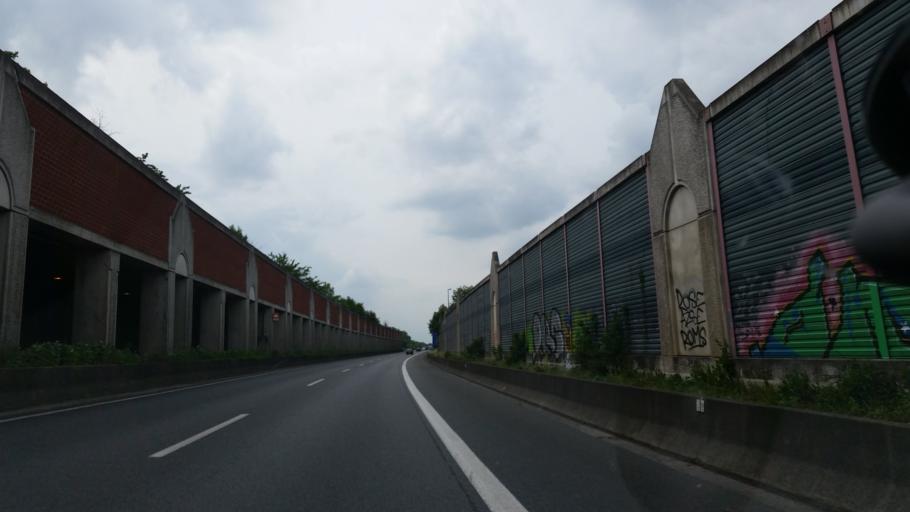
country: DE
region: Lower Saxony
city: Braunschweig
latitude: 52.2467
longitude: 10.5607
